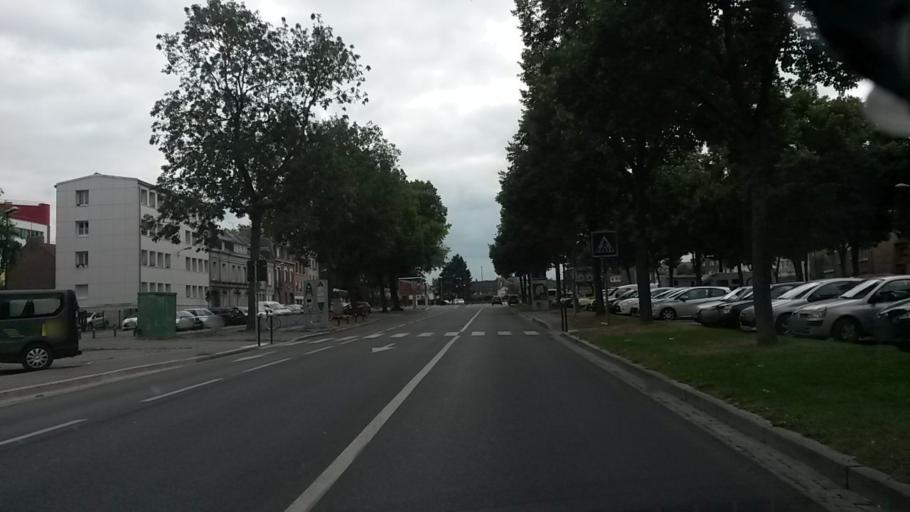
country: FR
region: Picardie
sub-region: Departement de la Somme
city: Amiens
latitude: 49.8945
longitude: 2.2872
